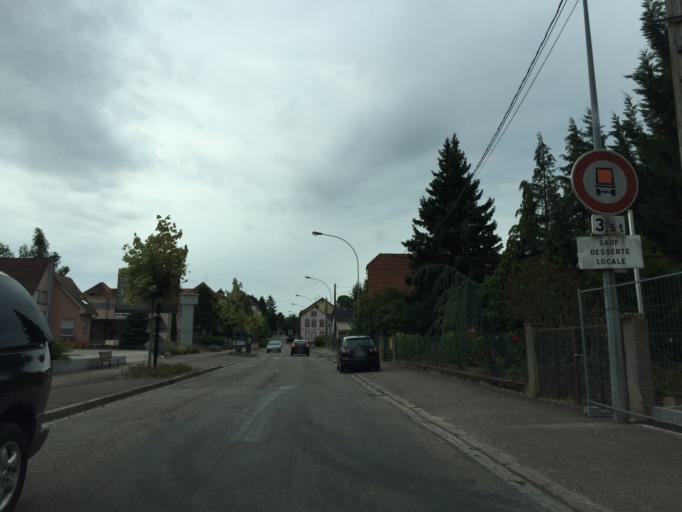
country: FR
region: Alsace
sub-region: Departement du Bas-Rhin
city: Wissembourg
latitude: 49.0326
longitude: 7.9452
